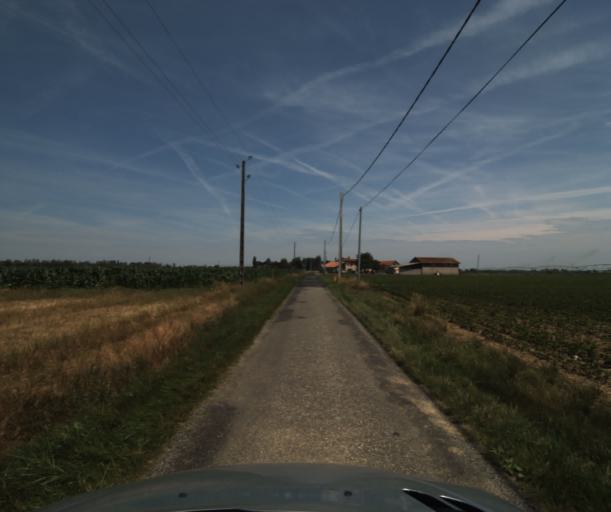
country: FR
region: Midi-Pyrenees
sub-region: Departement de la Haute-Garonne
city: Labastidette
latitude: 43.4448
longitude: 1.2478
